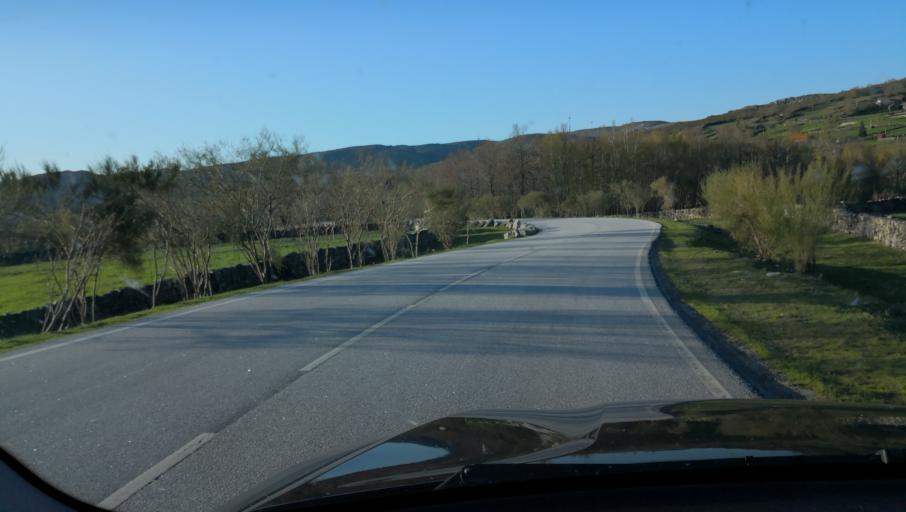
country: PT
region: Vila Real
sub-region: Vila Real
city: Vila Real
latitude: 41.3664
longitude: -7.8008
